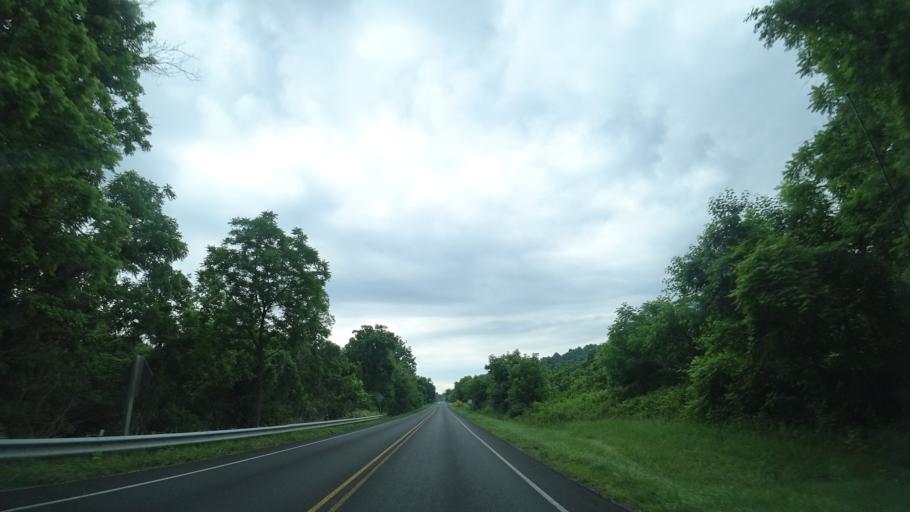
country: US
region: Virginia
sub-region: Warren County
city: Apple Mountain Lake
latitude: 38.9144
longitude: -78.1084
